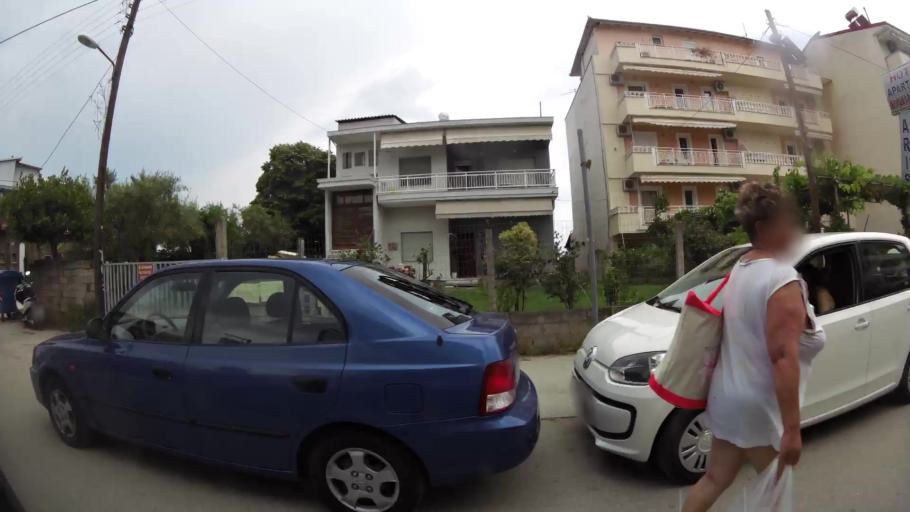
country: GR
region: Central Macedonia
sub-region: Nomos Pierias
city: Paralia
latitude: 40.2696
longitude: 22.5985
